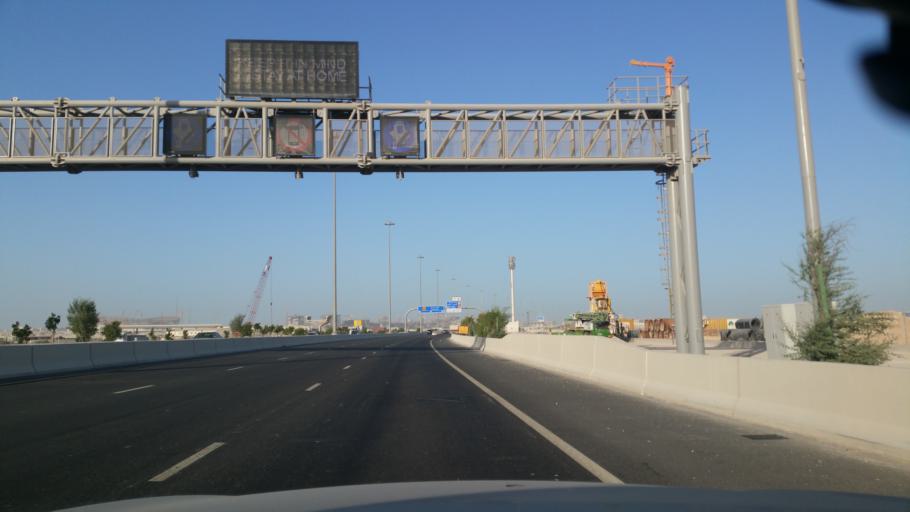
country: QA
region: Baladiyat Umm Salal
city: Umm Salal Muhammad
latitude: 25.3971
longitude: 51.4783
